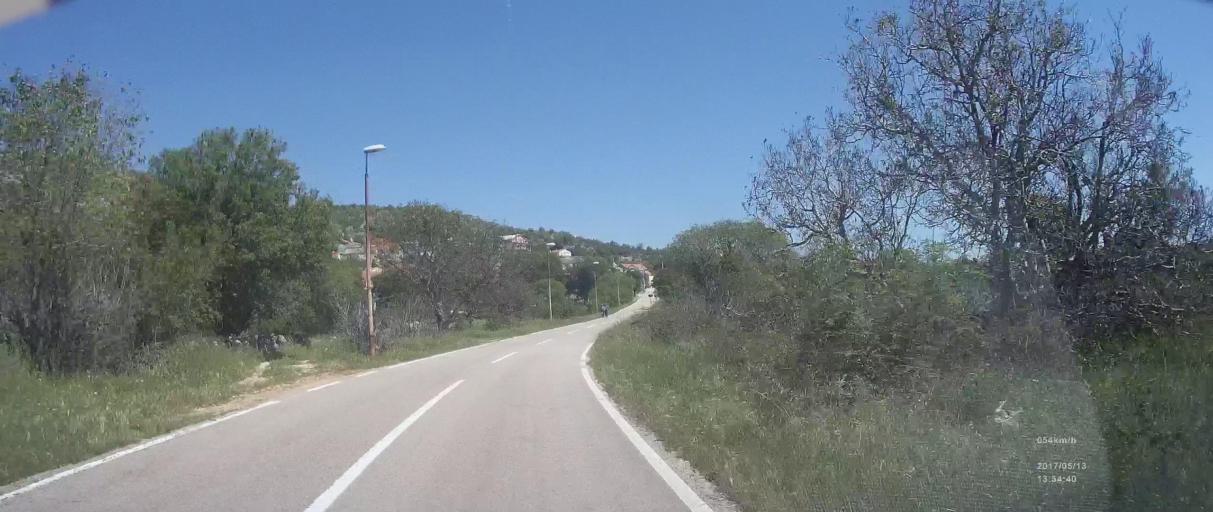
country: HR
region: Sibensko-Kniniska
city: Rogoznica
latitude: 43.5966
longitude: 16.0093
